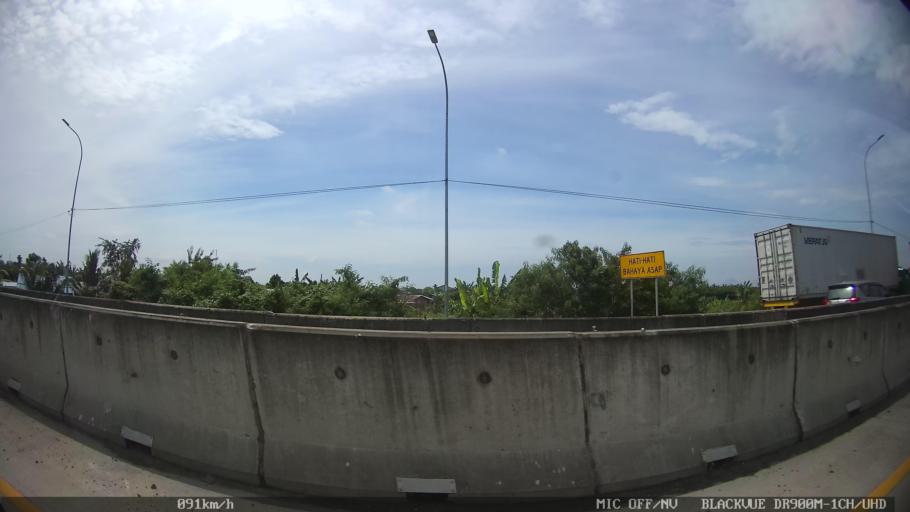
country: ID
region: North Sumatra
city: Medan
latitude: 3.6470
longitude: 98.6516
